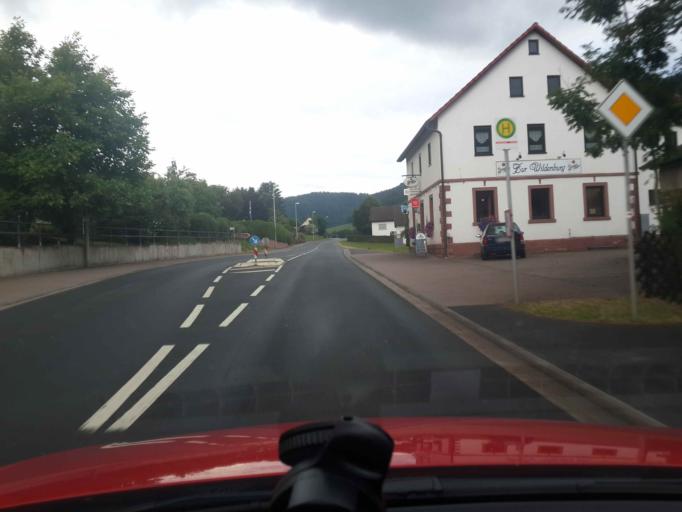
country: DE
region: Bavaria
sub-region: Regierungsbezirk Unterfranken
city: Kirchzell
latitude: 49.6159
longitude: 9.1998
